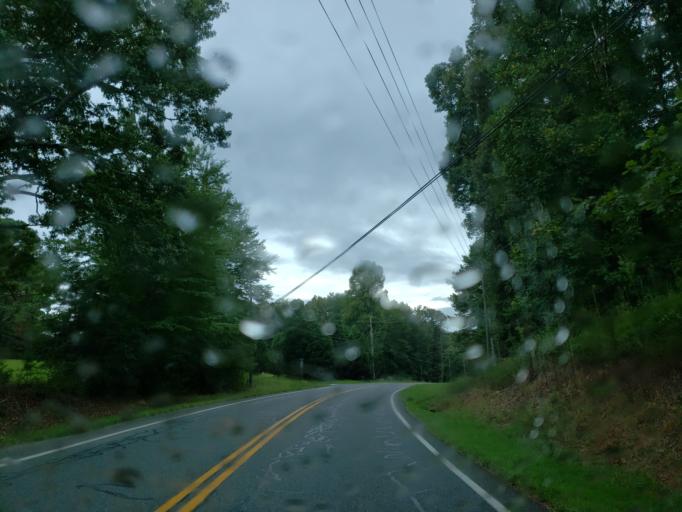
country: US
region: Georgia
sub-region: Gilmer County
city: Ellijay
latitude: 34.6232
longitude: -84.5782
